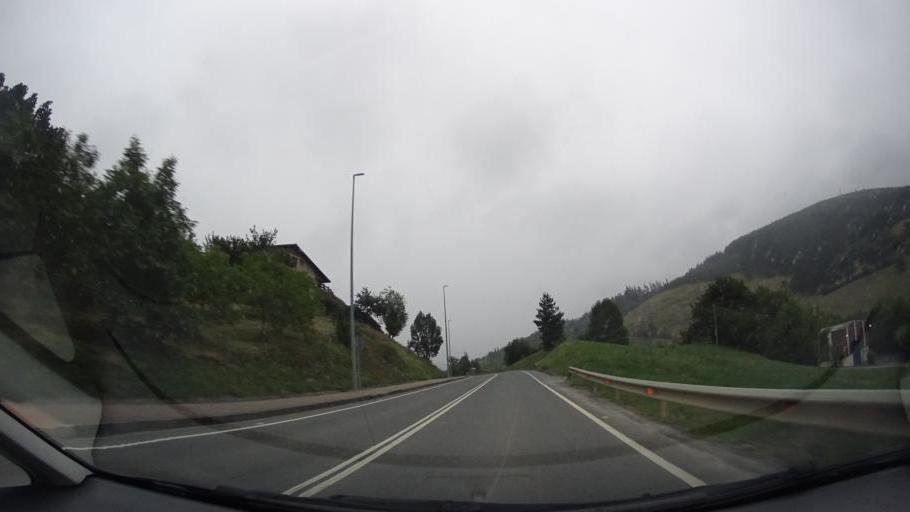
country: ES
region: Basque Country
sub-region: Bizkaia
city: Izurtza
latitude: 43.1448
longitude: -2.6473
